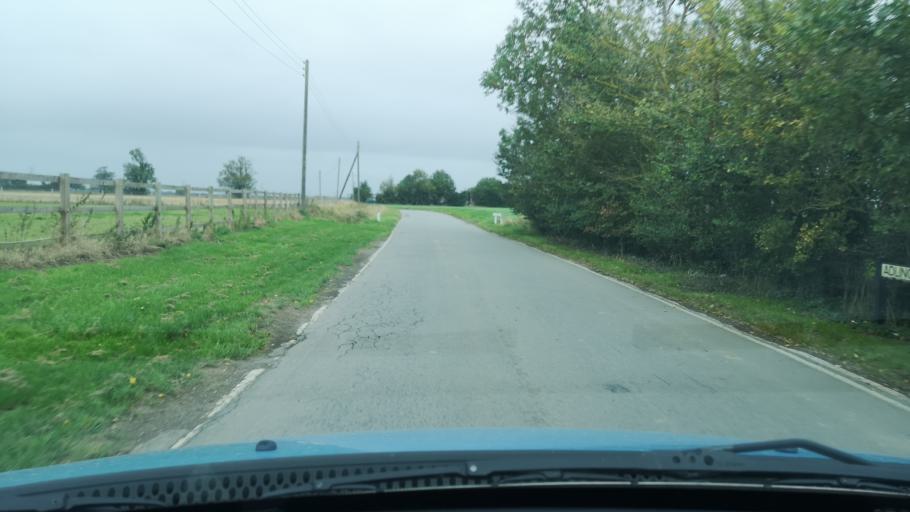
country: GB
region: England
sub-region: North Lincolnshire
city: Burton upon Stather
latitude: 53.6637
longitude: -0.7187
